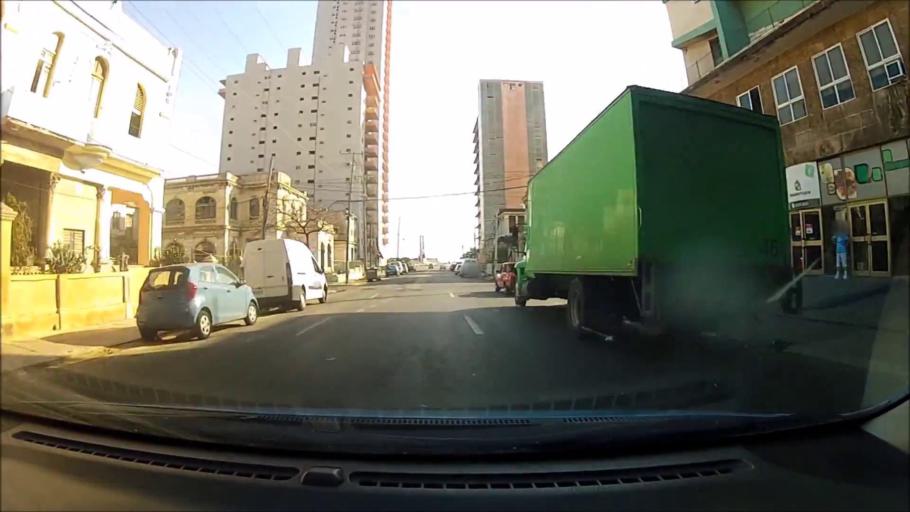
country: CU
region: La Habana
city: Havana
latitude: 23.1435
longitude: -82.3844
